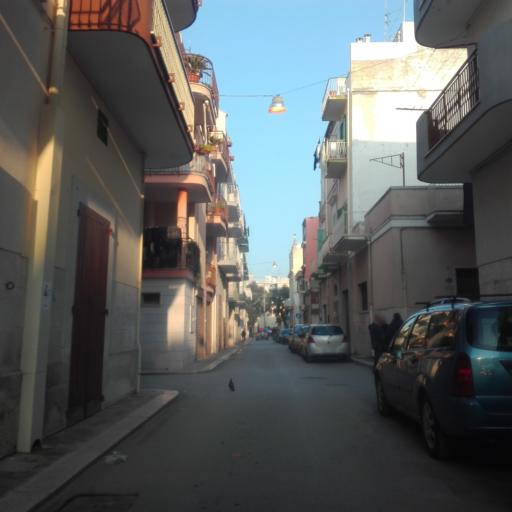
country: IT
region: Apulia
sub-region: Provincia di Bari
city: Corato
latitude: 41.1547
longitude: 16.4154
